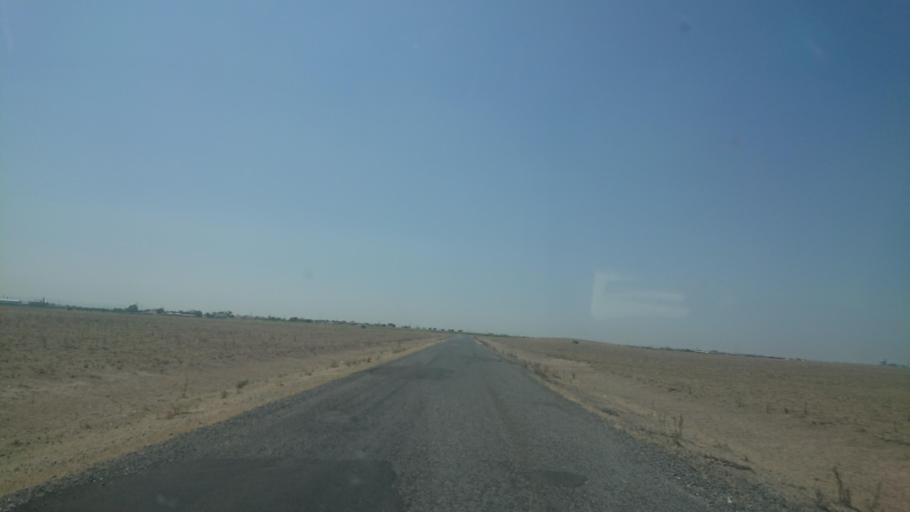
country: TR
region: Aksaray
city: Yesilova
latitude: 38.3021
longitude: 33.7319
